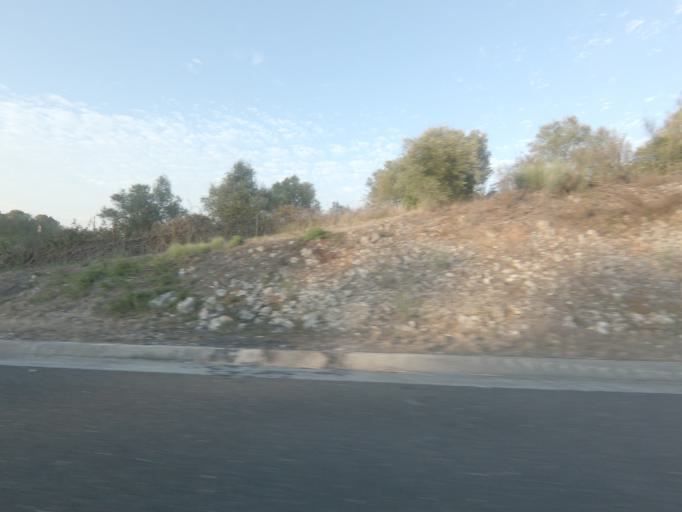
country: PT
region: Leiria
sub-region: Leiria
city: Santa Catarina da Serra
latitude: 39.6942
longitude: -8.6932
